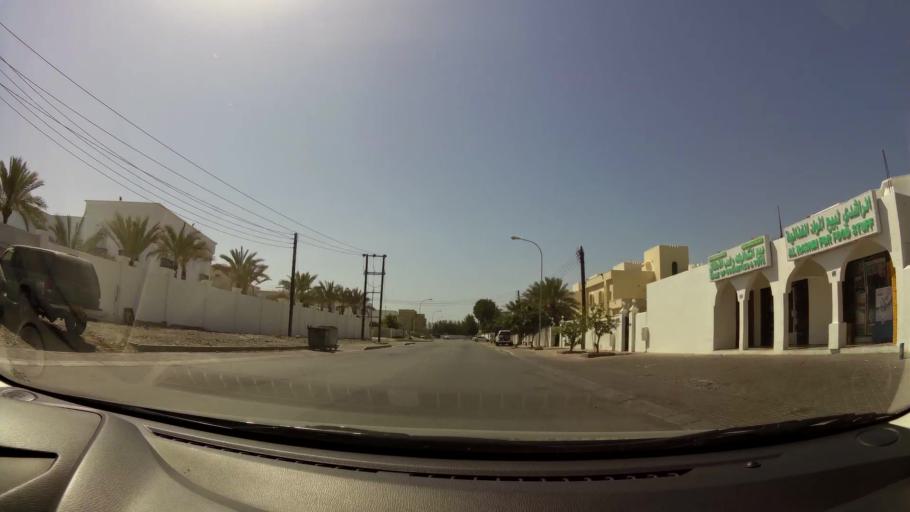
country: OM
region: Muhafazat Masqat
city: As Sib al Jadidah
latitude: 23.6353
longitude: 58.2183
